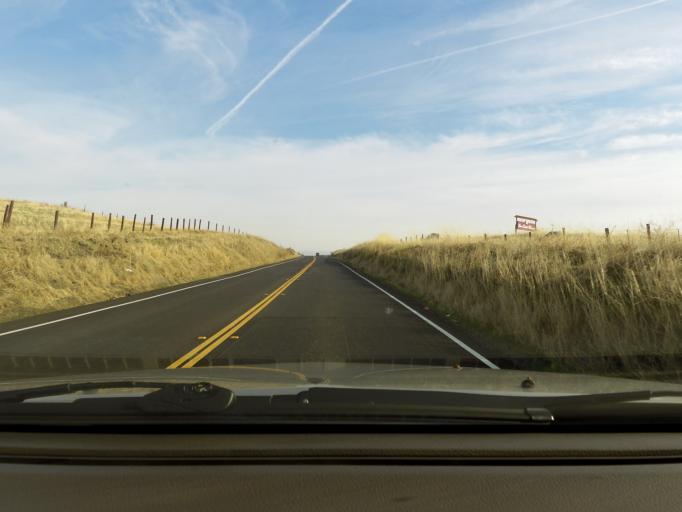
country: US
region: California
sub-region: Madera County
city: Bonadelle Ranchos-Madera Ranchos
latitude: 37.0420
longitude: -119.7794
